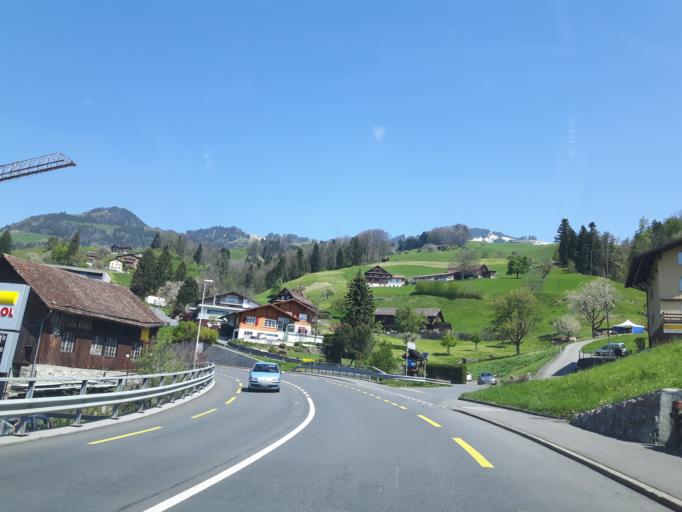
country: CH
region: Schwyz
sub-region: Bezirk Schwyz
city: Schwyz
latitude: 47.0332
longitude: 8.6455
